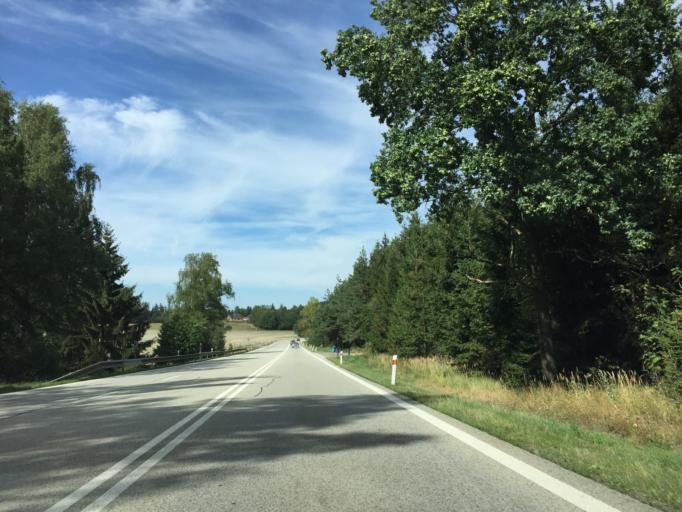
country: CZ
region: Central Bohemia
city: Votice
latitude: 49.6059
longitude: 14.6600
